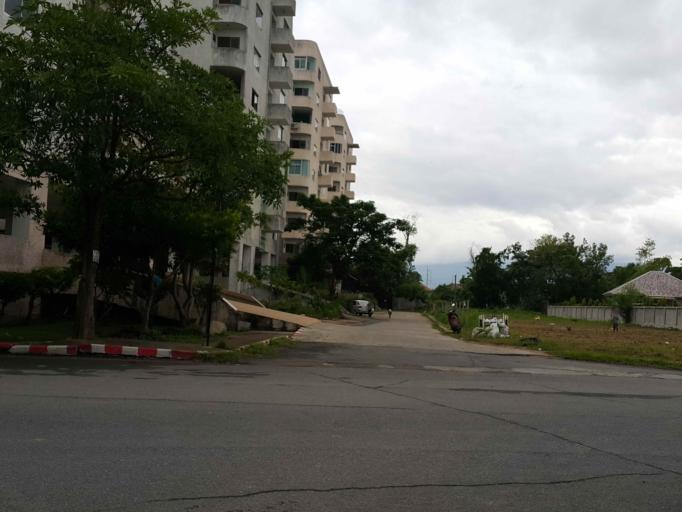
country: TH
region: Chiang Mai
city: San Sai
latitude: 18.8294
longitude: 99.0549
